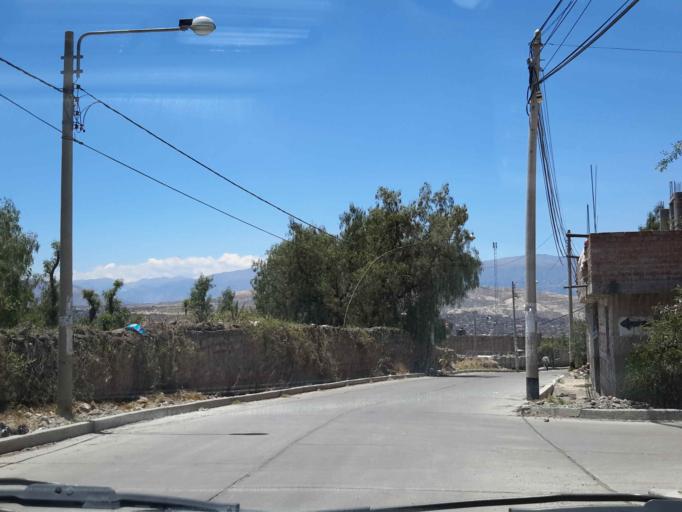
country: PE
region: Ayacucho
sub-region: Provincia de Huamanga
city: Carmen Alto
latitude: -13.1707
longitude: -74.2246
